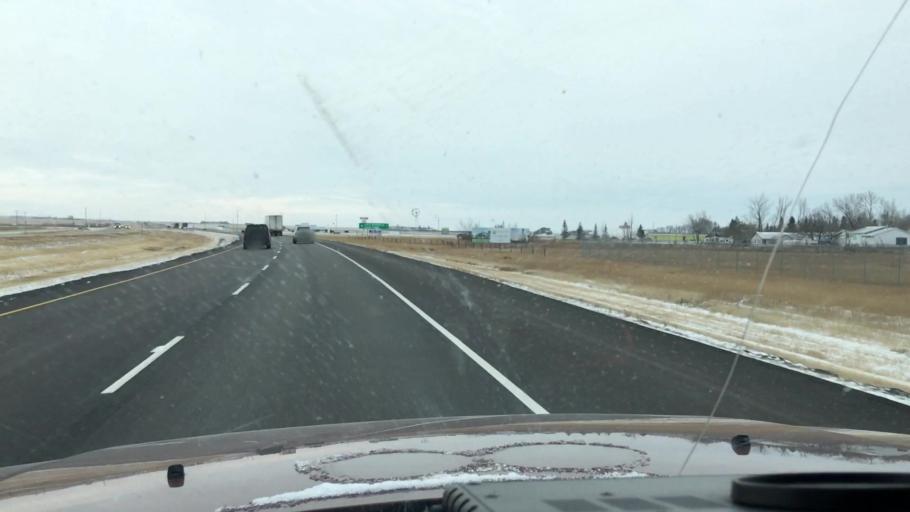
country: CA
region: Saskatchewan
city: Saskatoon
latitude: 51.8139
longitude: -106.4978
